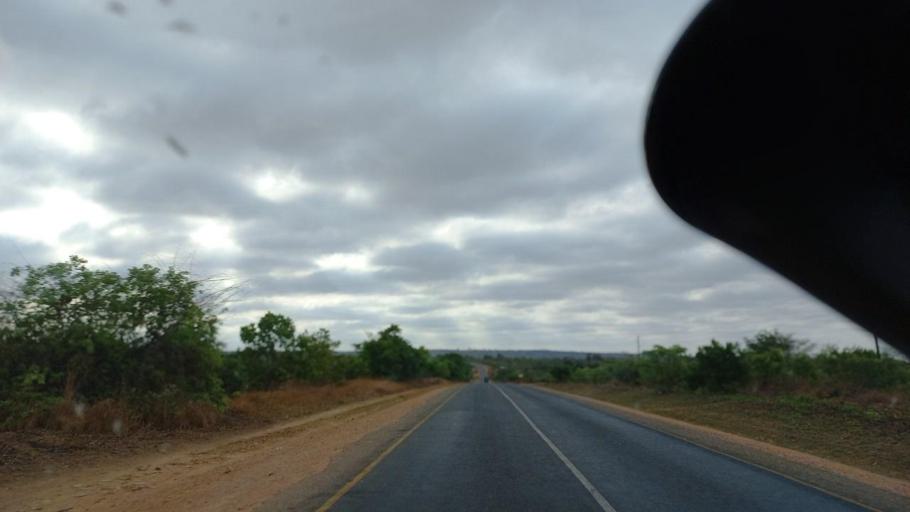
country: ZM
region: Lusaka
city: Chongwe
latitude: -15.2875
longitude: 28.7968
